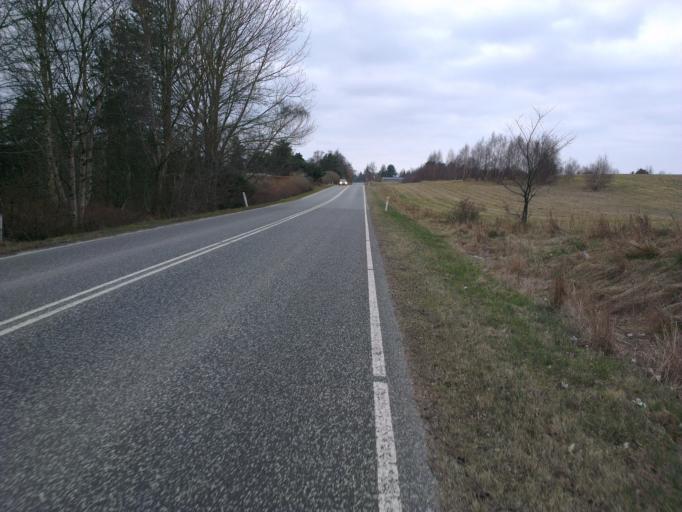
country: DK
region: Capital Region
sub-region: Frederikssund Kommune
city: Jaegerspris
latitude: 55.9172
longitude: 11.9244
